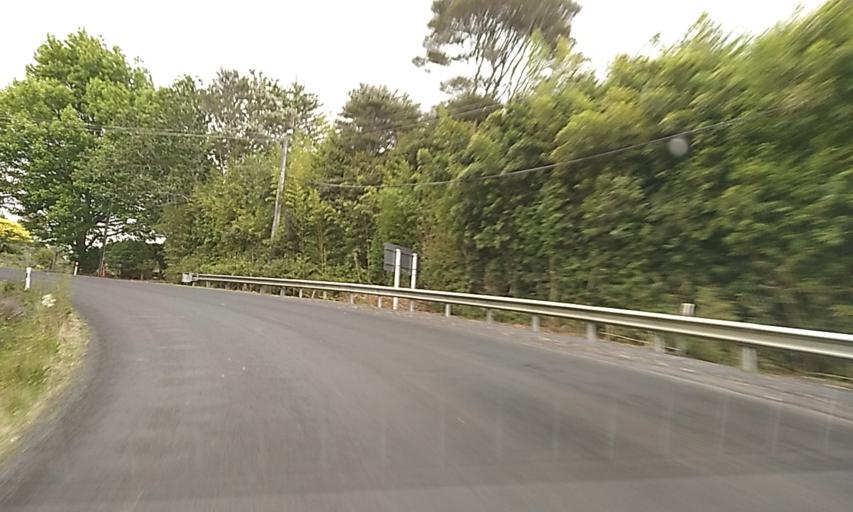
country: NZ
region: Auckland
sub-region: Auckland
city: Pukekohe East
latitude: -37.2973
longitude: 174.9423
